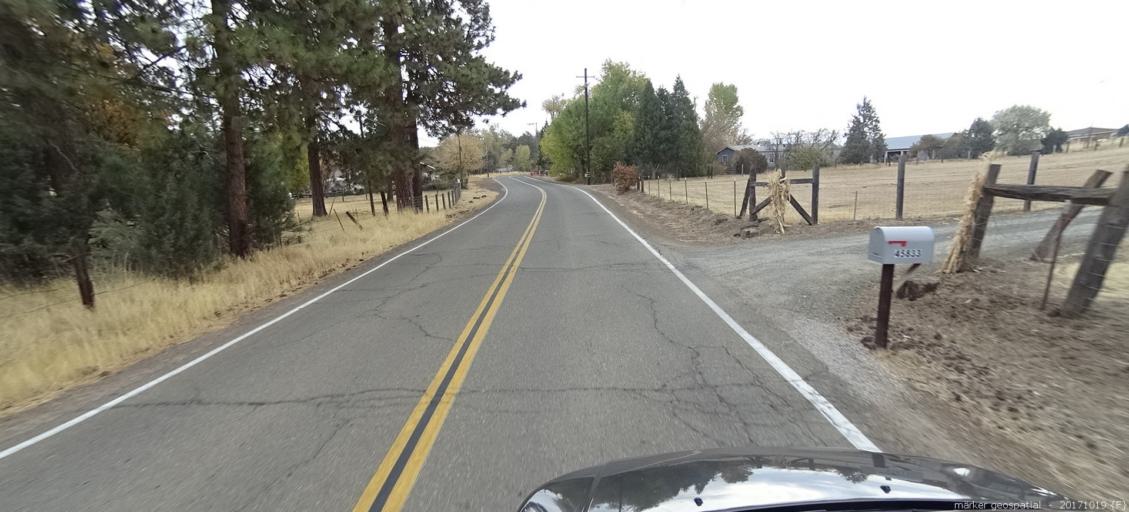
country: US
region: California
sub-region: Shasta County
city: Burney
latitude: 41.0497
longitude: -121.3379
